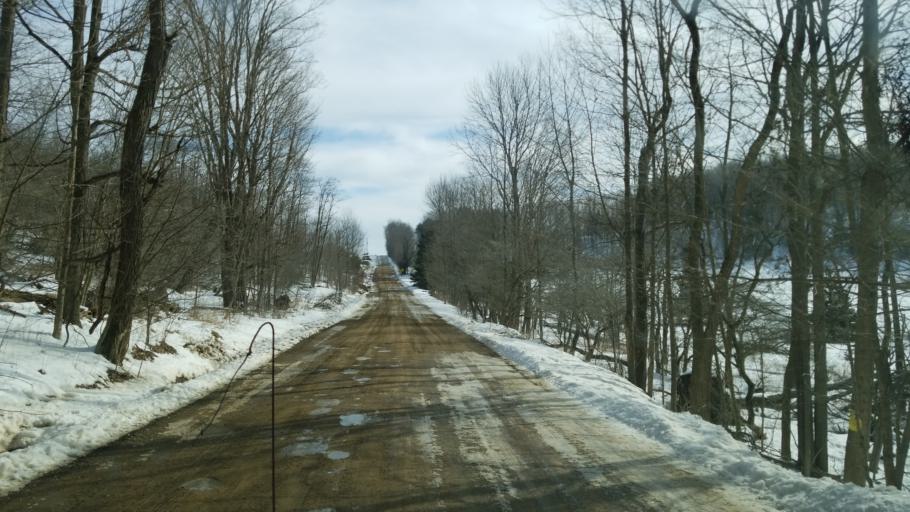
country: US
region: New York
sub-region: Allegany County
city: Andover
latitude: 42.0112
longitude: -77.8053
